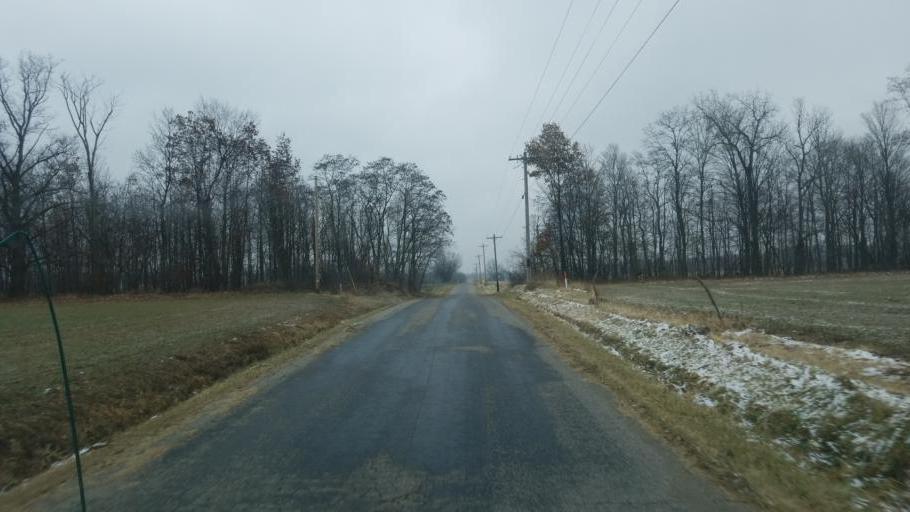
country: US
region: Ohio
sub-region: Huron County
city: New London
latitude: 41.0160
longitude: -82.3484
